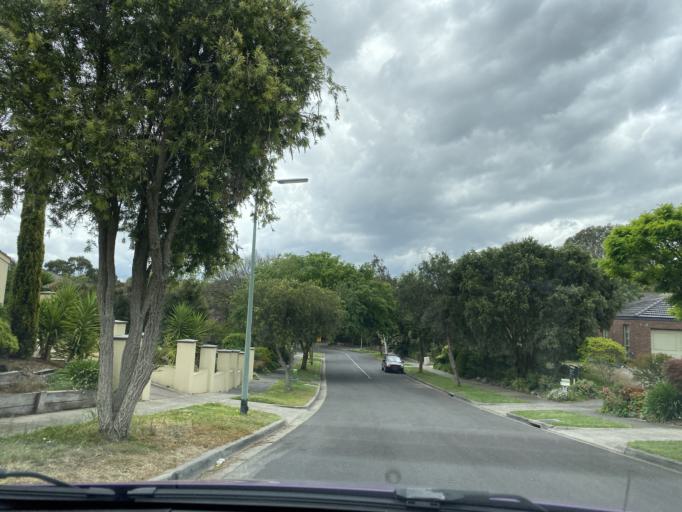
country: AU
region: Victoria
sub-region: Manningham
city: Templestowe Lower
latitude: -37.7678
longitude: 145.1356
